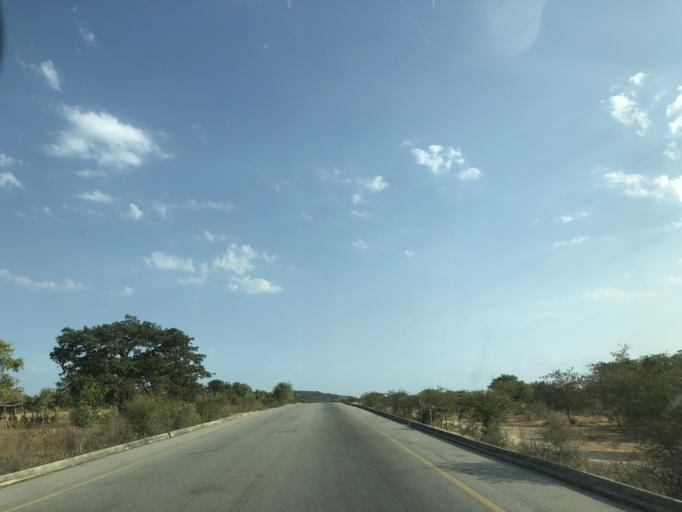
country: AO
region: Benguela
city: Benguela
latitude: -13.2235
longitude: 13.7677
